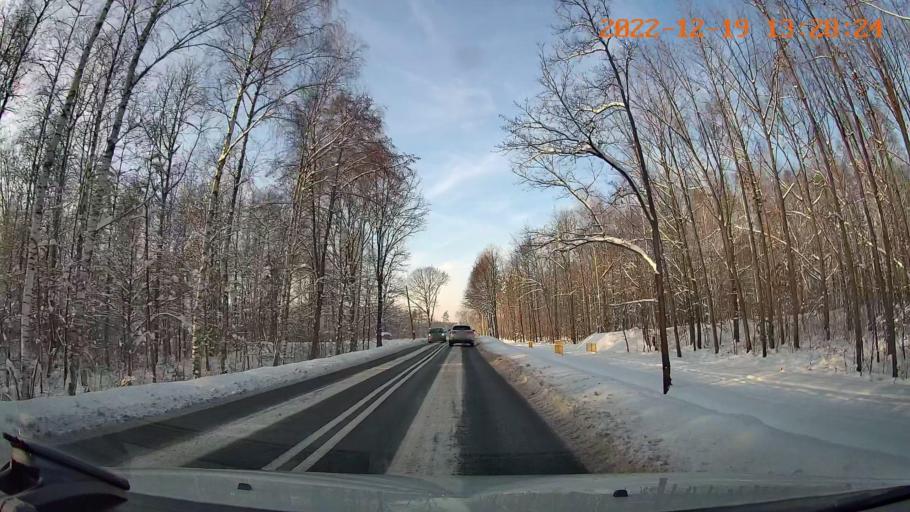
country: PL
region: Silesian Voivodeship
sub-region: Powiat bierunsko-ledzinski
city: Ledziny
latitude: 50.1117
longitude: 19.1284
